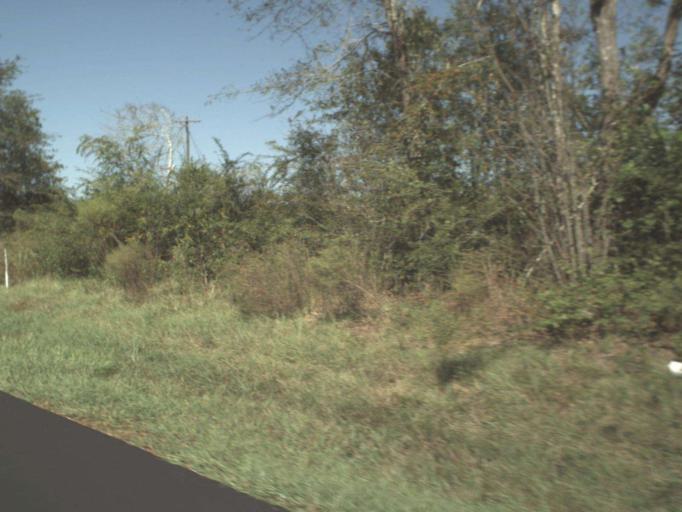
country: US
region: Florida
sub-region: Walton County
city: DeFuniak Springs
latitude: 30.8196
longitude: -86.2120
